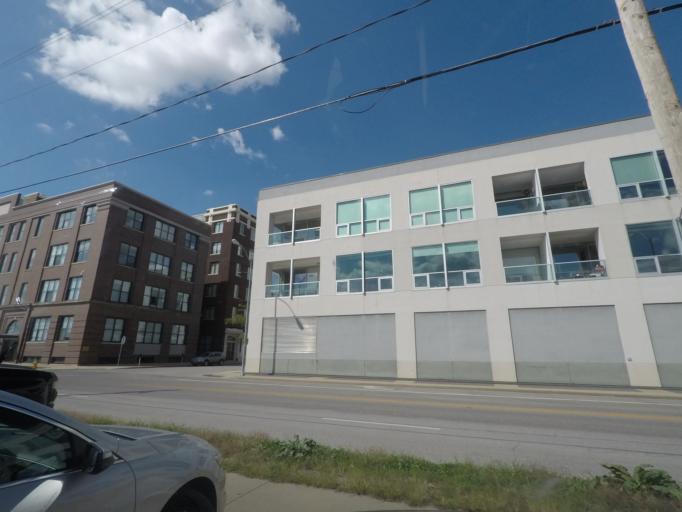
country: US
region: Iowa
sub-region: Polk County
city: Des Moines
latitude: 41.5830
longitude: -93.6285
